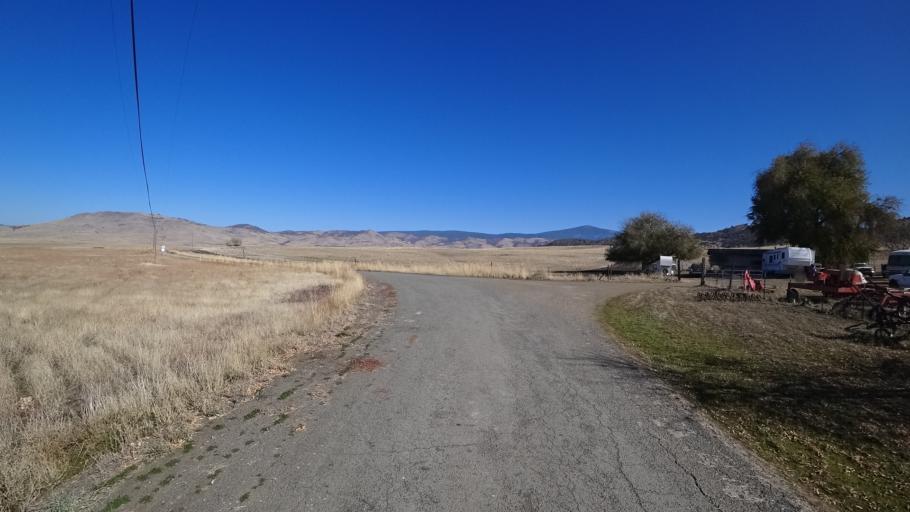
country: US
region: California
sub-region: Siskiyou County
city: Montague
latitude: 41.7942
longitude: -122.4177
